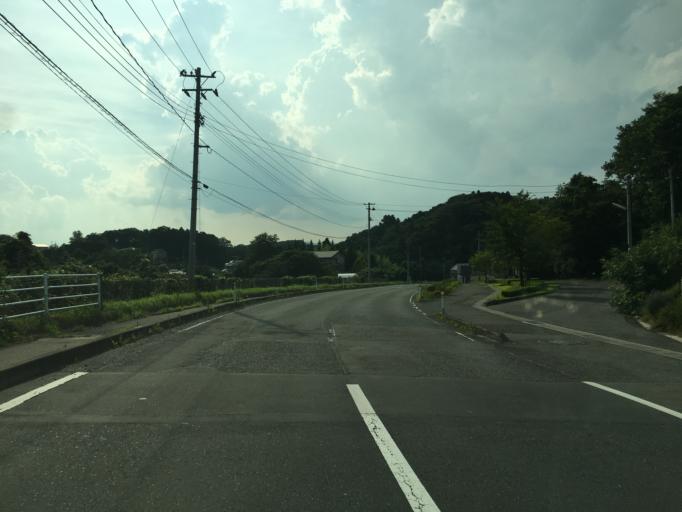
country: JP
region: Fukushima
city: Miharu
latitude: 37.4463
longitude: 140.4336
